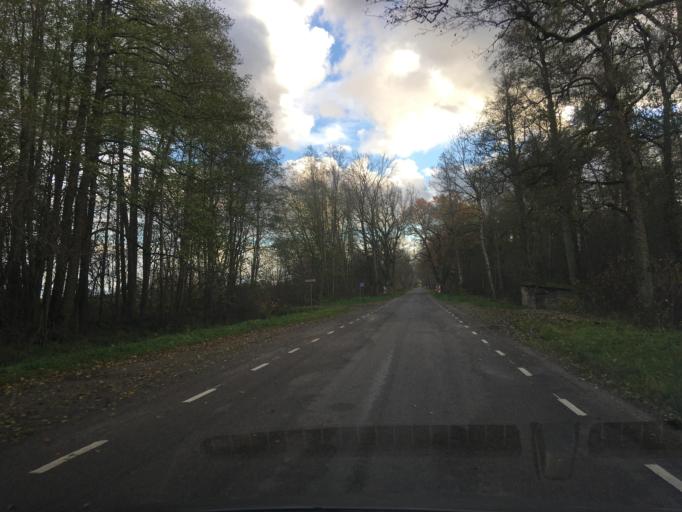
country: EE
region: Harju
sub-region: Maardu linn
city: Maardu
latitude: 59.4360
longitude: 25.0167
